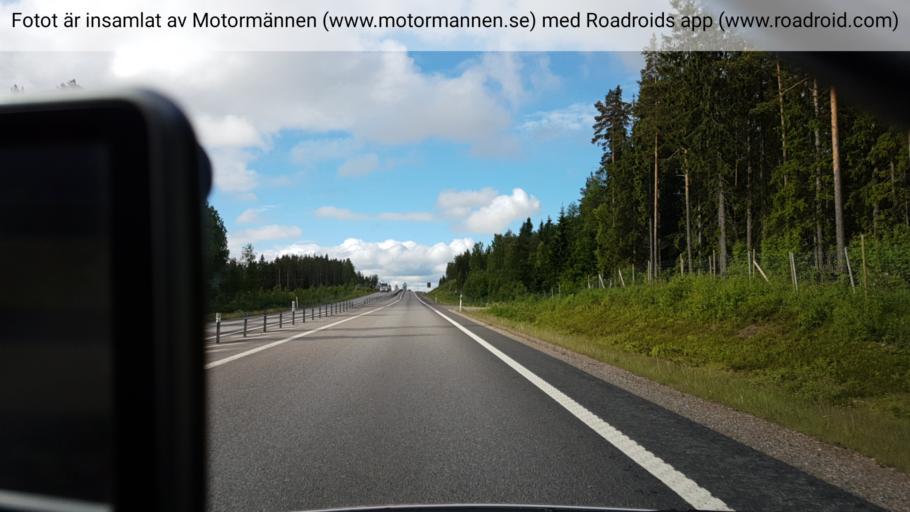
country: SE
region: Vaesternorrland
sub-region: Sundsvalls Kommun
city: Njurundabommen
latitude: 62.1225
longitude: 17.3306
